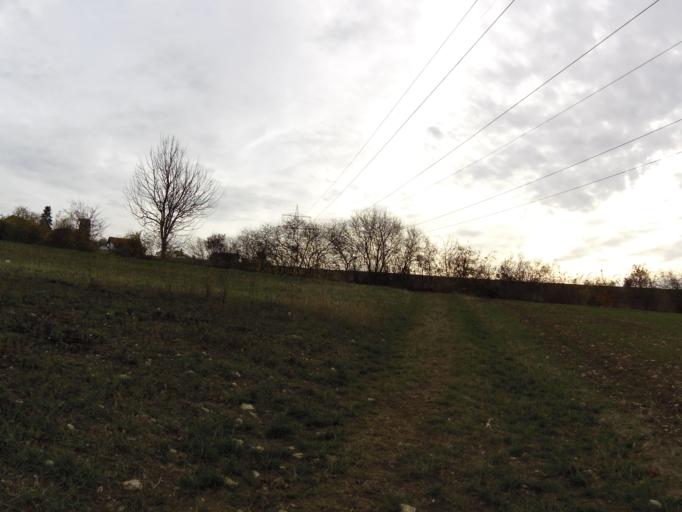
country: DE
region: Bavaria
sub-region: Regierungsbezirk Unterfranken
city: Kist
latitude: 49.7448
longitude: 9.8323
